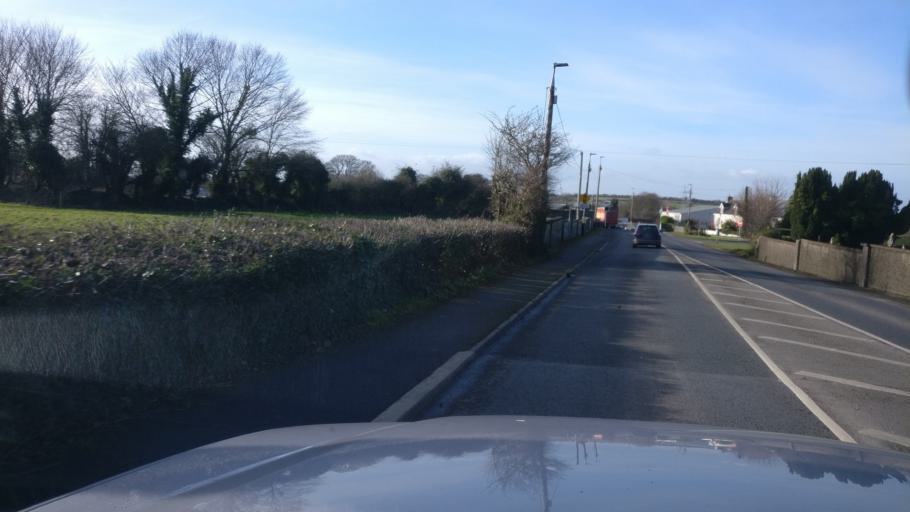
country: IE
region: Leinster
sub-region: Uibh Fhaili
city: Tullamore
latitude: 53.2133
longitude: -7.4459
